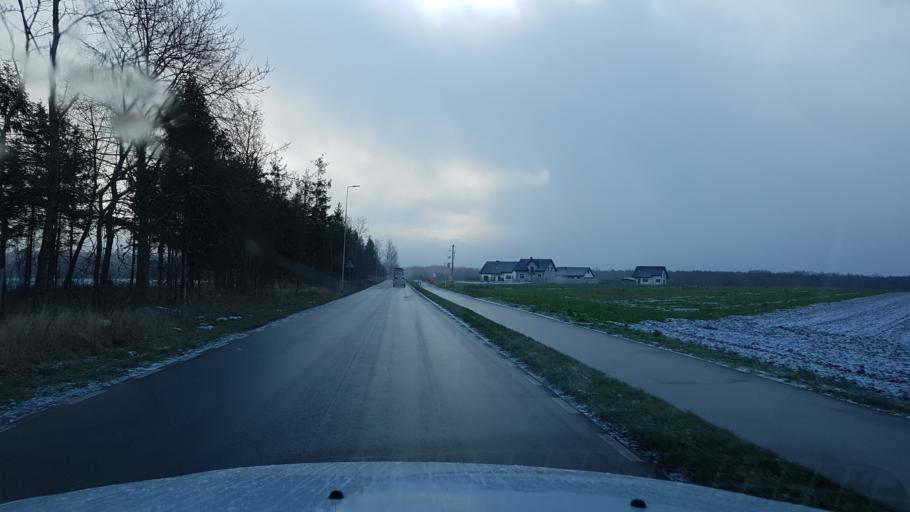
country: PL
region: West Pomeranian Voivodeship
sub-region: Powiat gryficki
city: Trzebiatow
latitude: 54.0562
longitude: 15.2993
